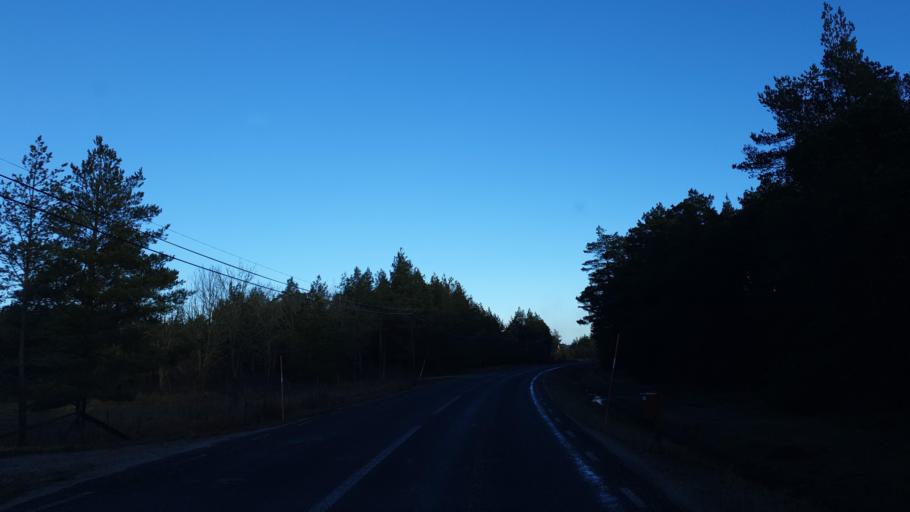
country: SE
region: Gotland
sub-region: Gotland
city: Slite
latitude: 57.4673
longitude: 18.7077
